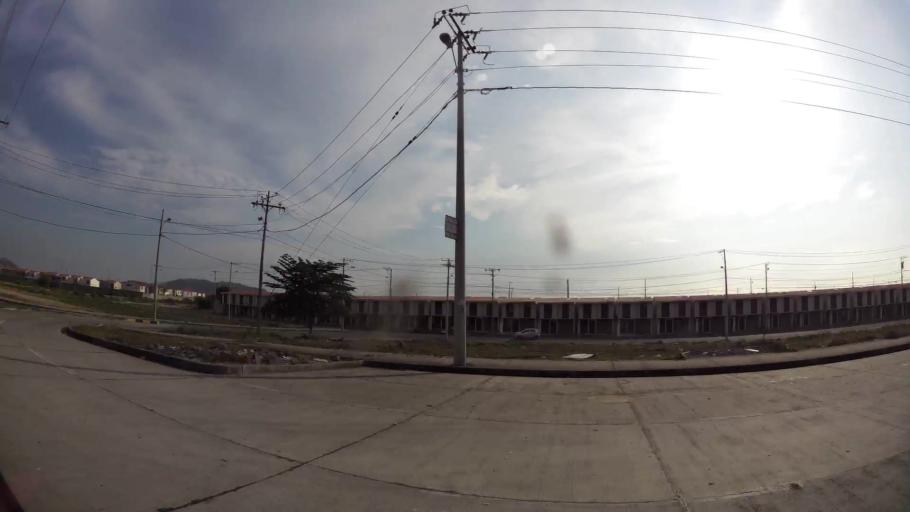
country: EC
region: Guayas
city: Eloy Alfaro
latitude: -2.0676
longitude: -79.9009
